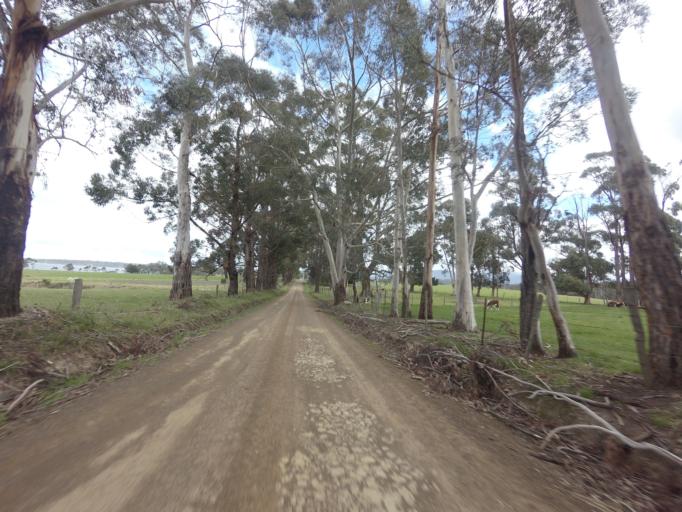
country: AU
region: Tasmania
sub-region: Huon Valley
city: Geeveston
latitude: -43.4287
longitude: 146.9931
